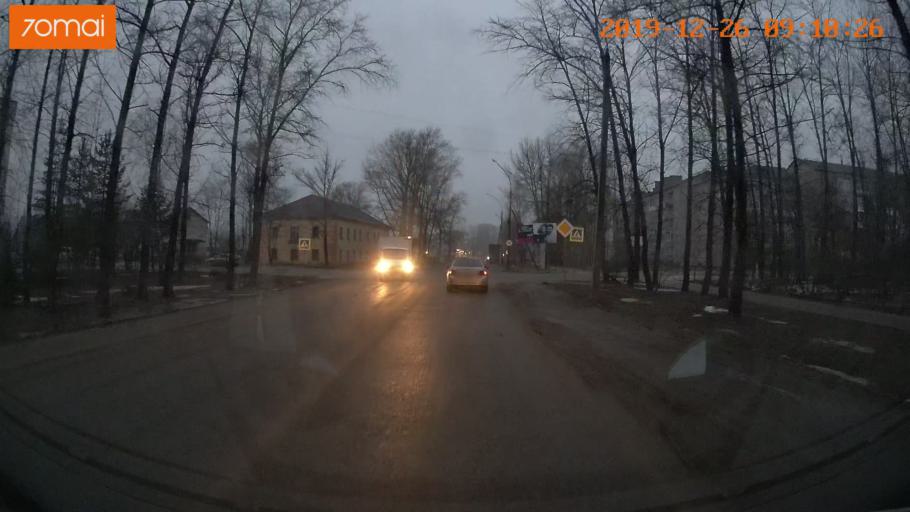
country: RU
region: Vologda
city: Gryazovets
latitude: 58.8709
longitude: 40.2527
